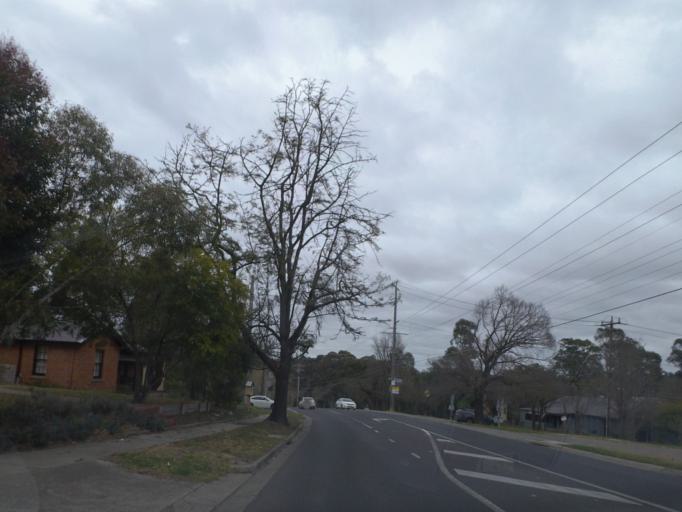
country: AU
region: Victoria
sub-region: Nillumbik
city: Eltham
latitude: -37.7221
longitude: 145.1457
